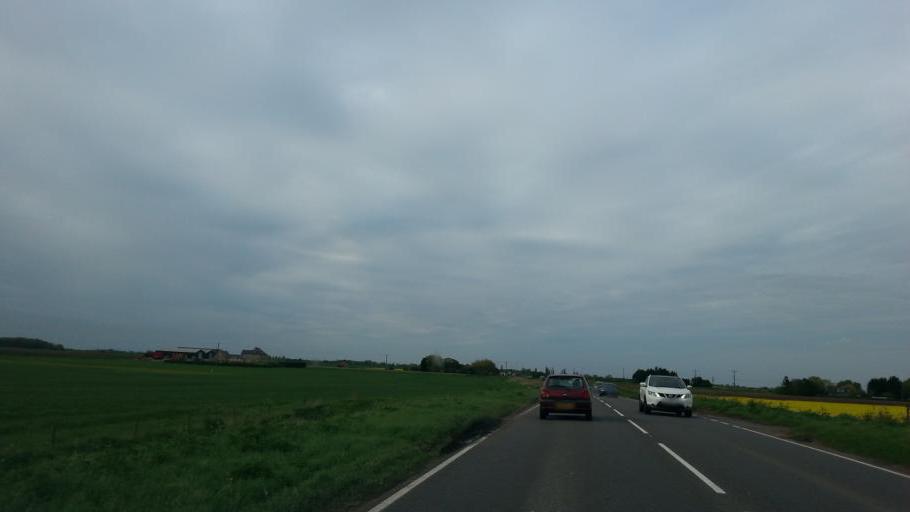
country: GB
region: England
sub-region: Cambridgeshire
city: March
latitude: 52.5851
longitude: 0.0580
